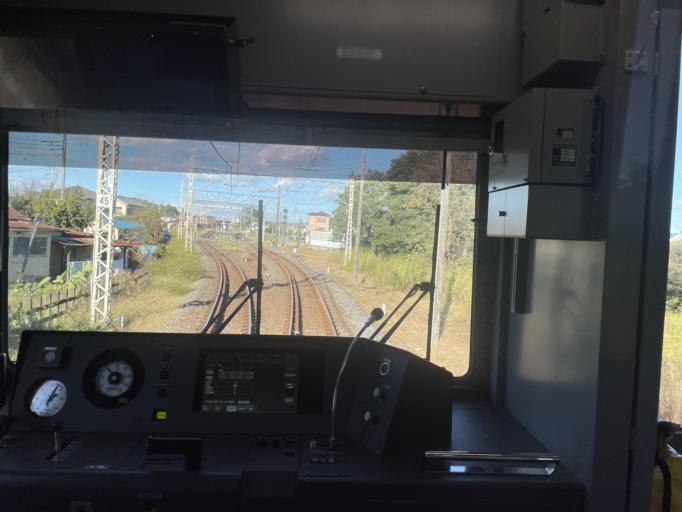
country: JP
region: Tochigi
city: Mibu
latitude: 36.4211
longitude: 139.8040
